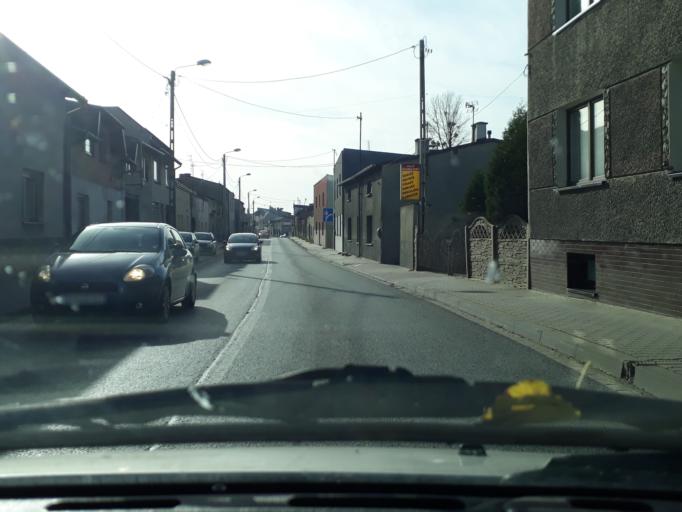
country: PL
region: Silesian Voivodeship
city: Wozniki
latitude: 50.5899
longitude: 19.0618
